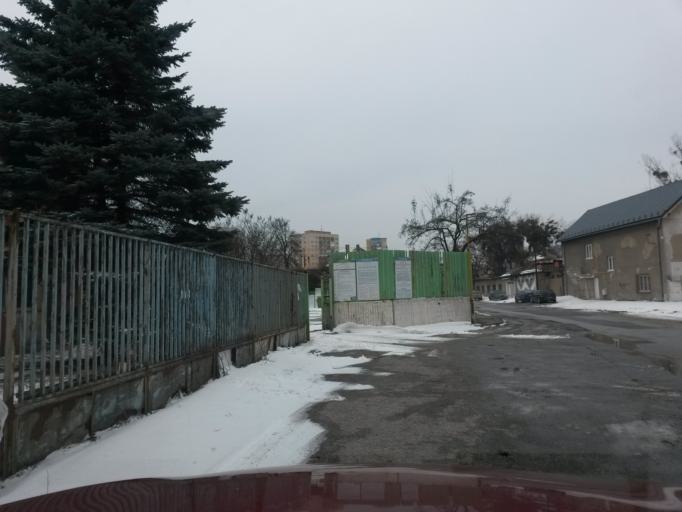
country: SK
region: Kosicky
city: Kosice
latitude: 48.7122
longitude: 21.2692
